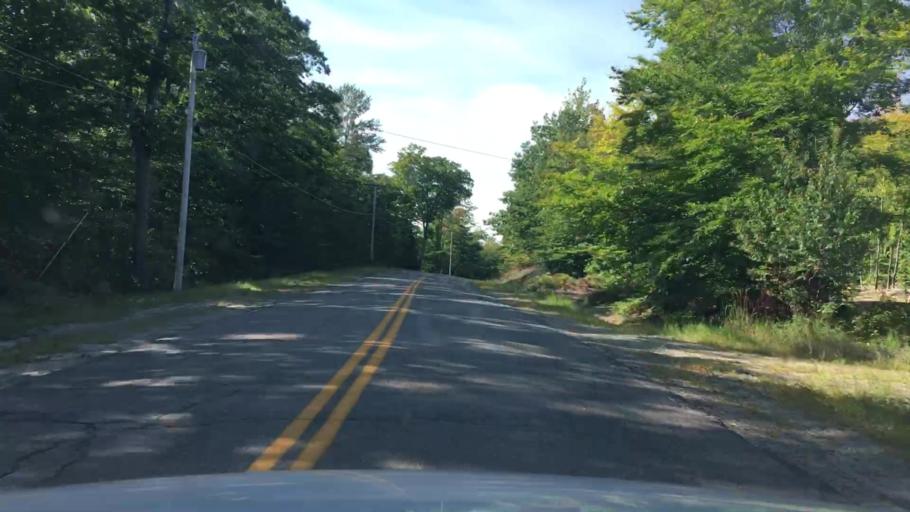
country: US
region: Maine
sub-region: Penobscot County
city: Enfield
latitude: 45.2250
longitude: -68.5397
